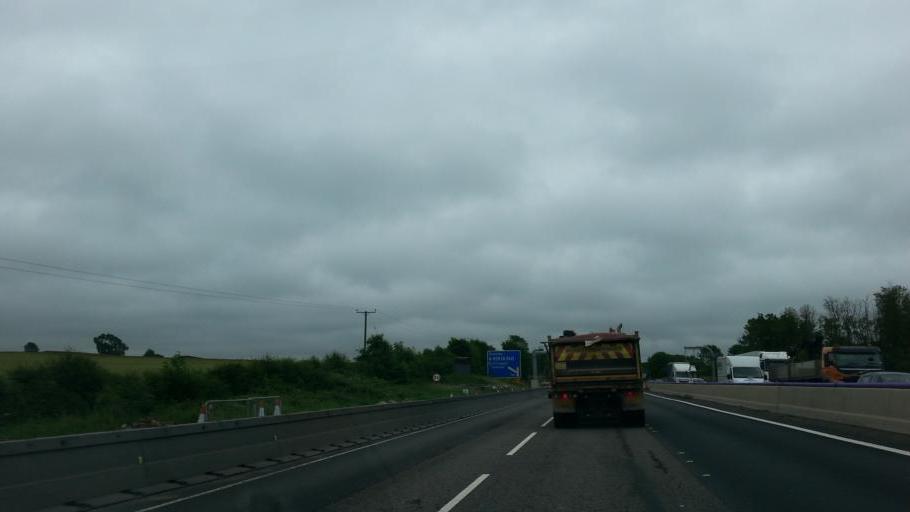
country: GB
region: England
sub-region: Leicestershire
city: Lutterworth
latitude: 52.3720
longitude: -1.1621
